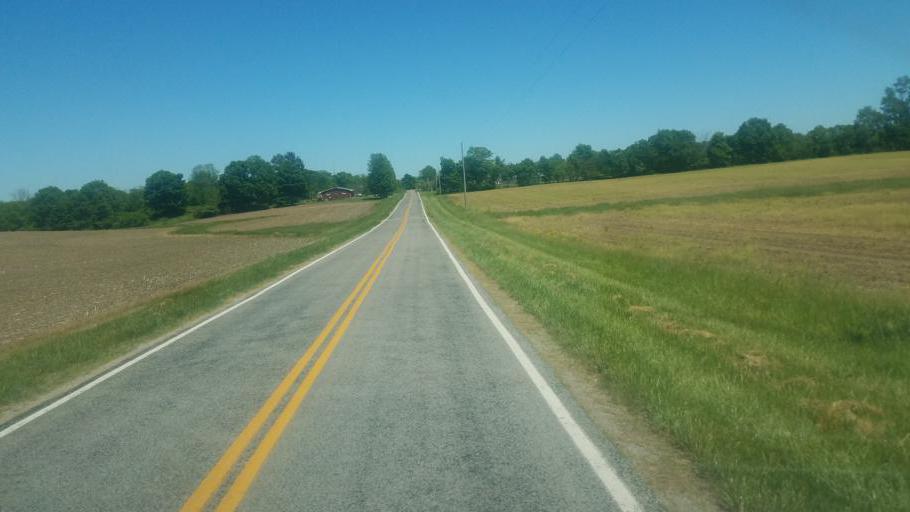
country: US
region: Ohio
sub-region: Champaign County
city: Saint Paris
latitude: 40.2072
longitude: -84.0080
